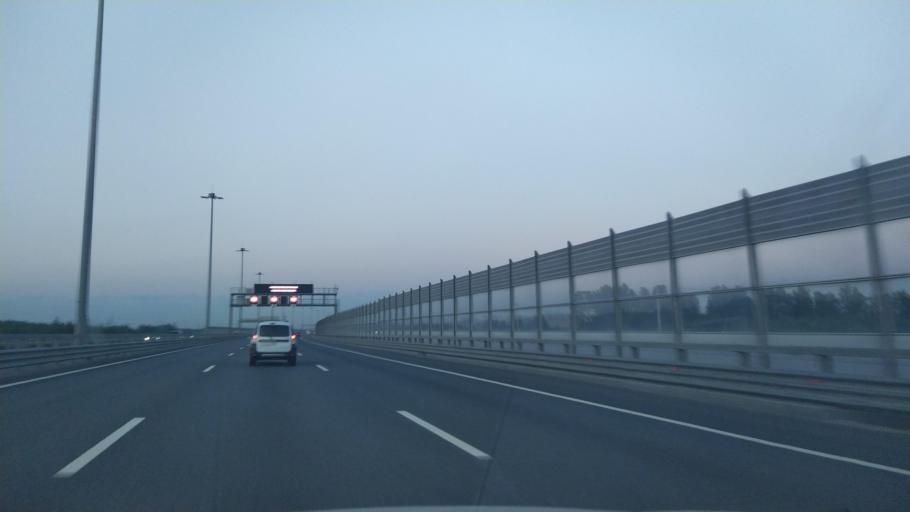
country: RU
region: St.-Petersburg
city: Pargolovo
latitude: 60.0990
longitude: 30.2895
